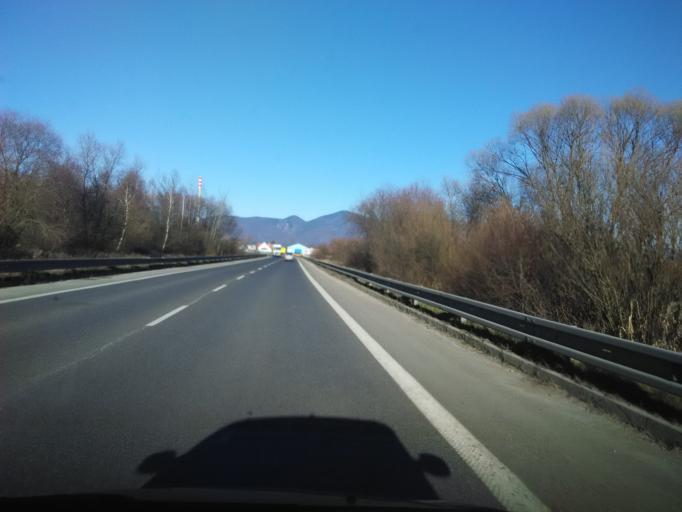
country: SK
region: Zilinsky
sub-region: Okres Martin
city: Martin
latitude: 49.0463
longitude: 18.9073
